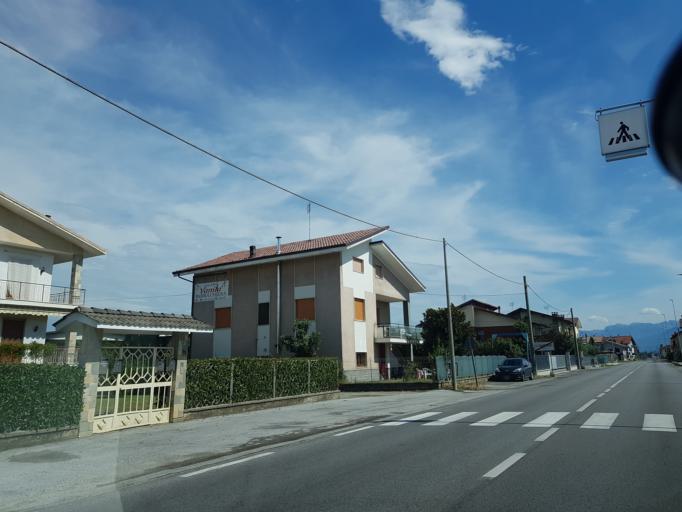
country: IT
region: Piedmont
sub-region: Provincia di Cuneo
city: Tarantasca
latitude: 44.4801
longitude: 7.5053
